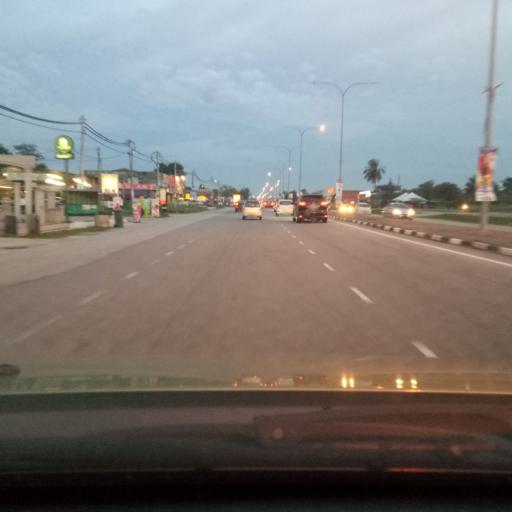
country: MY
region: Kedah
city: Alor Setar
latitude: 6.0966
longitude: 100.3767
